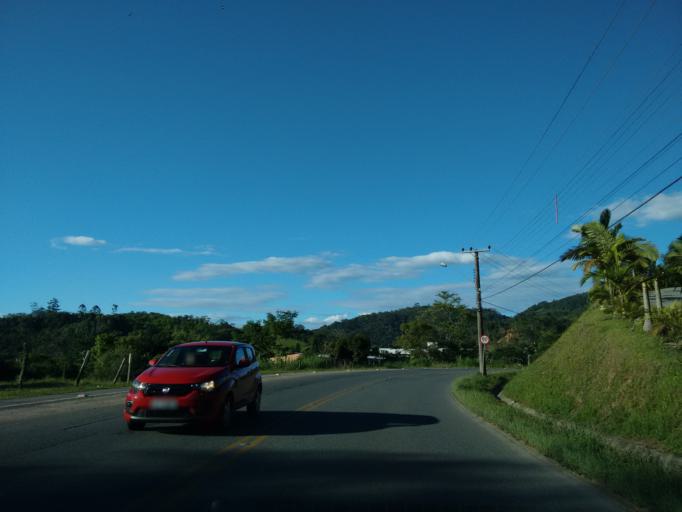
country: BR
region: Santa Catarina
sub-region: Pomerode
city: Pomerode
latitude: -26.7500
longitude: -49.1654
